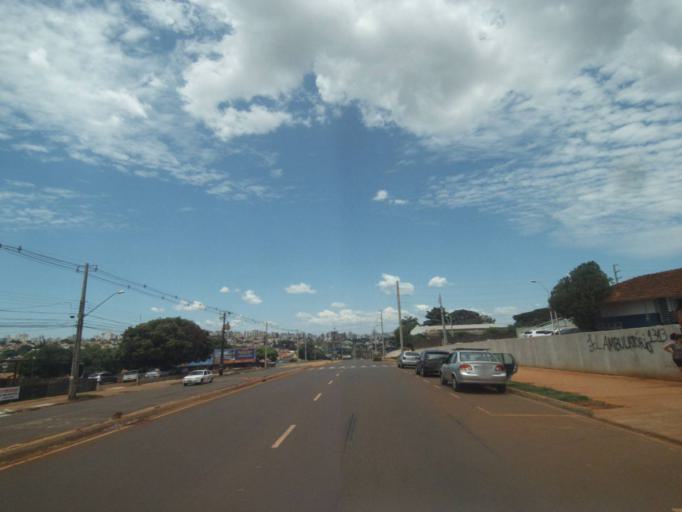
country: BR
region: Parana
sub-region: Londrina
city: Londrina
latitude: -23.3213
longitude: -51.1892
